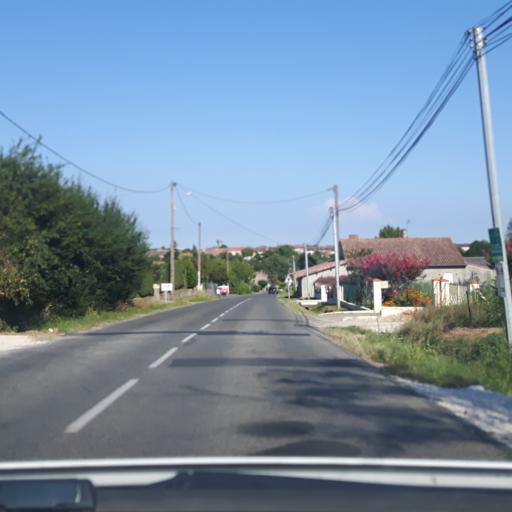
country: FR
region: Midi-Pyrenees
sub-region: Departement de la Haute-Garonne
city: Fronton
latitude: 43.8418
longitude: 1.3800
